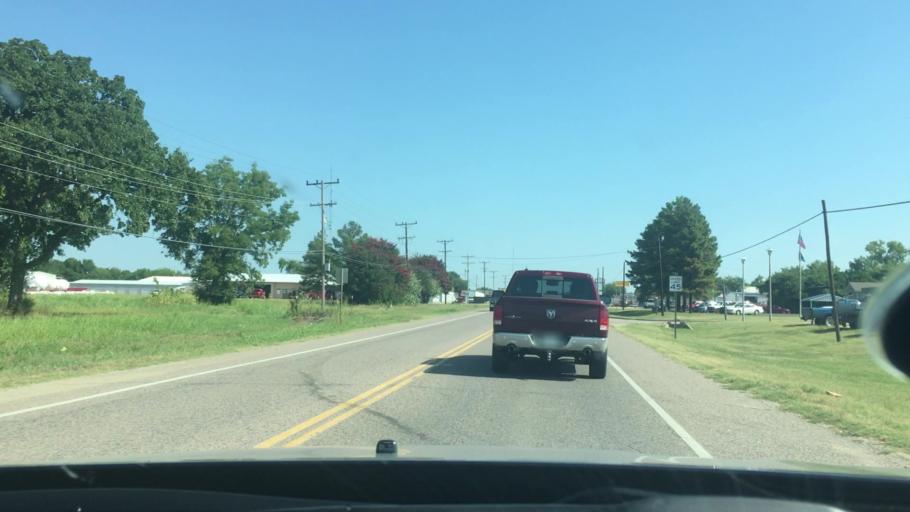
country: US
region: Oklahoma
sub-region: Bryan County
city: Durant
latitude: 34.0146
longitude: -96.3730
